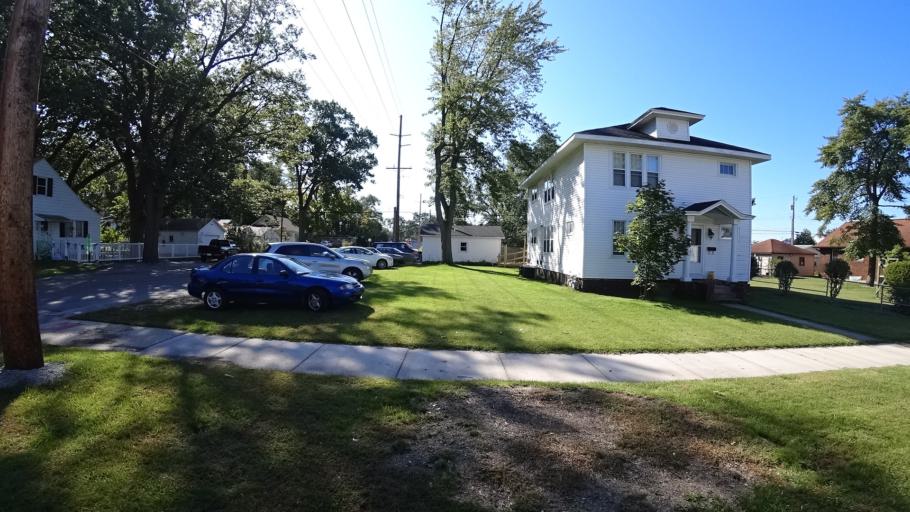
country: US
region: Indiana
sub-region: LaPorte County
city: Michigan City
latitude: 41.7024
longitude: -86.8908
